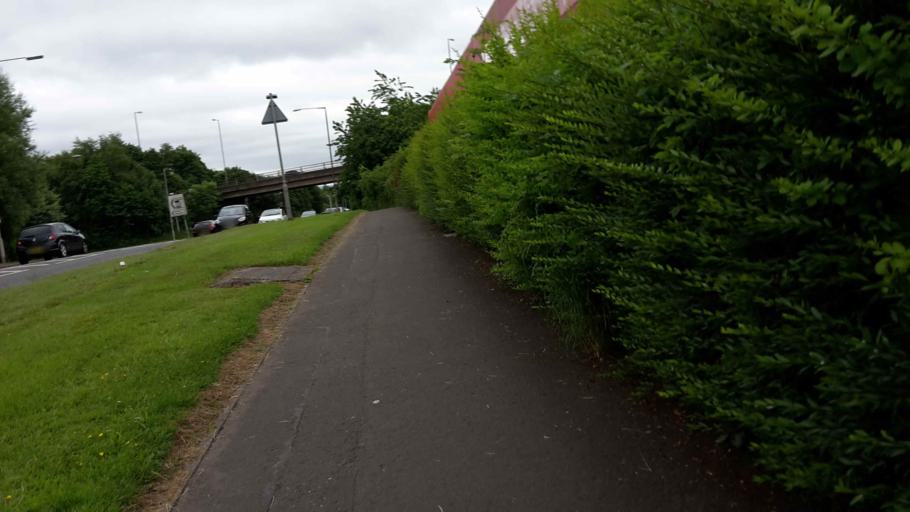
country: GB
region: Scotland
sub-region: South Lanarkshire
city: Bothwell
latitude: 55.7910
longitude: -4.0822
